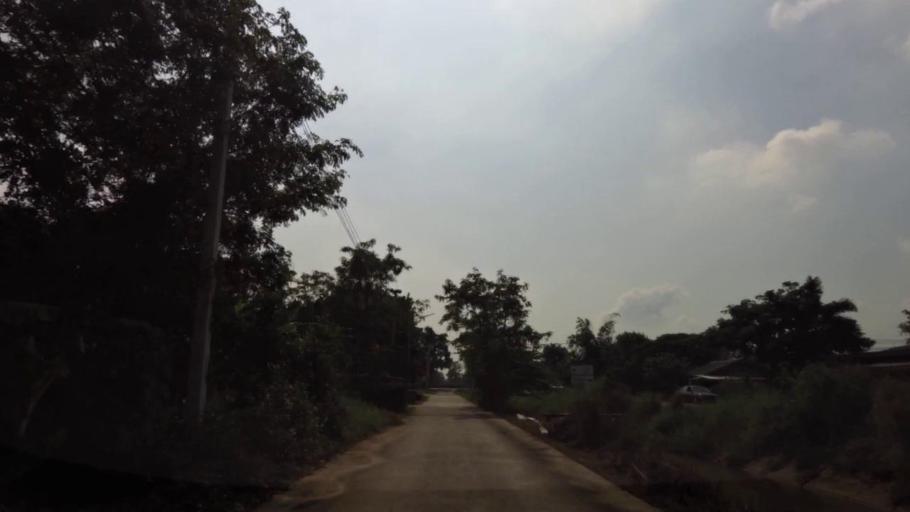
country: TH
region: Ang Thong
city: Wiset Chaichan
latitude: 14.6039
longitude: 100.3944
